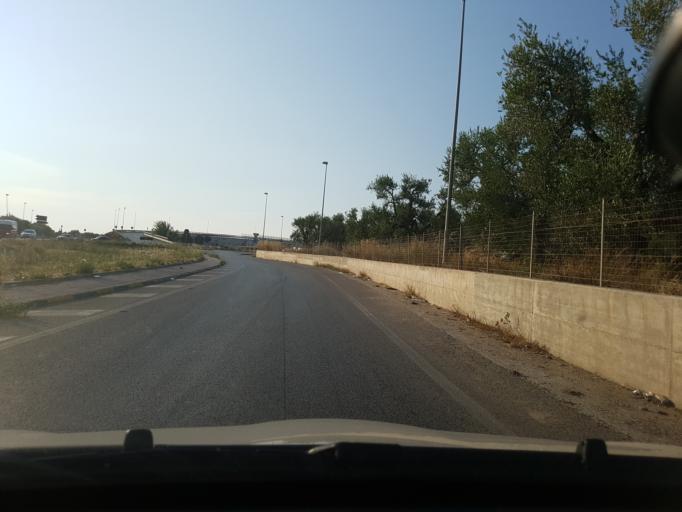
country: IT
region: Apulia
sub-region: Provincia di Foggia
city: Cerignola
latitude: 41.2728
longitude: 15.8769
